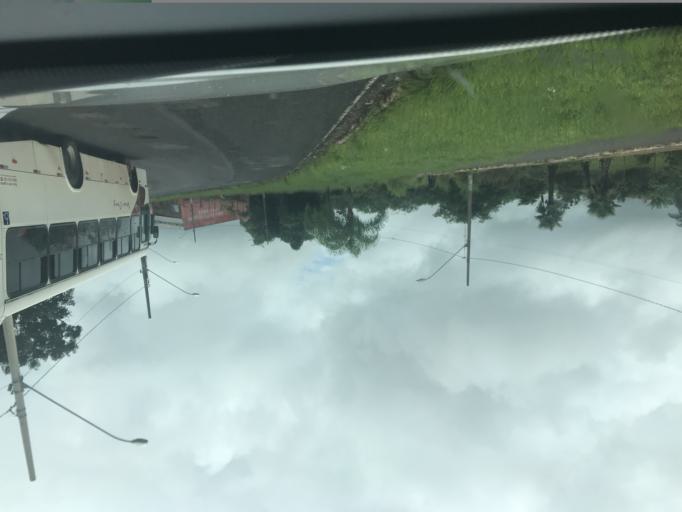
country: BR
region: Minas Gerais
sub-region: Araxa
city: Araxa
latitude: -19.5803
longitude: -46.9395
